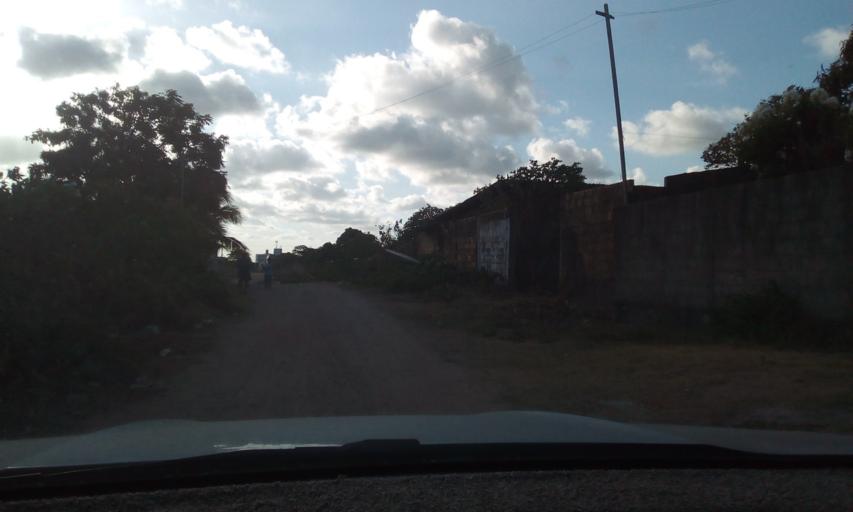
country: BR
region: Paraiba
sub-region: Joao Pessoa
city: Joao Pessoa
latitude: -7.1504
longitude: -34.8102
